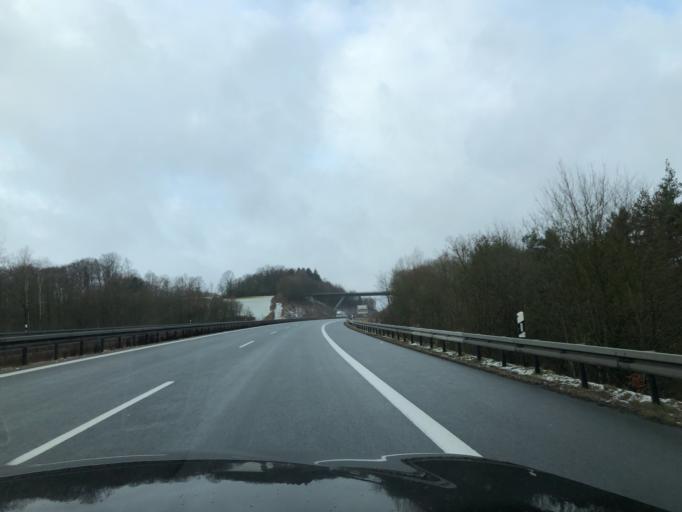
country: DE
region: Bavaria
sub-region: Upper Palatinate
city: Ursensollen
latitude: 49.3979
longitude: 11.7922
